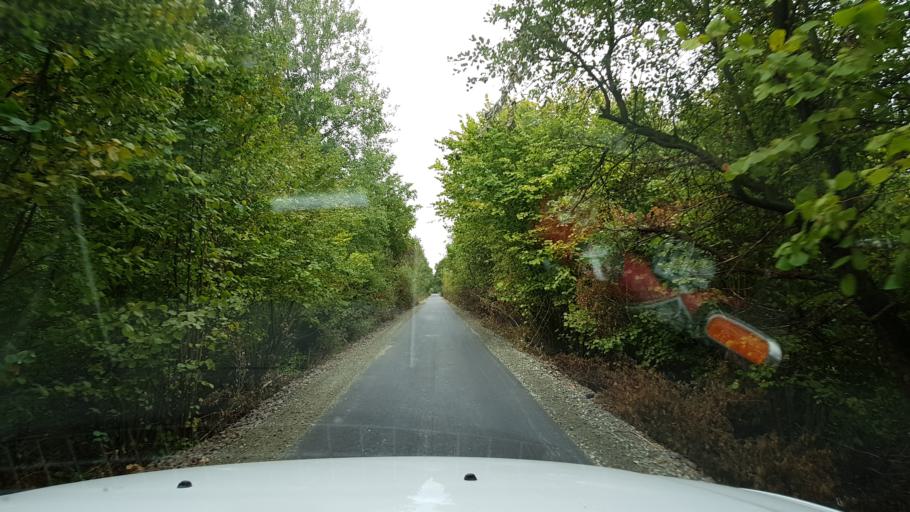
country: PL
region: West Pomeranian Voivodeship
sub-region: Powiat gryfinski
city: Moryn
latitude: 52.8825
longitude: 14.4277
